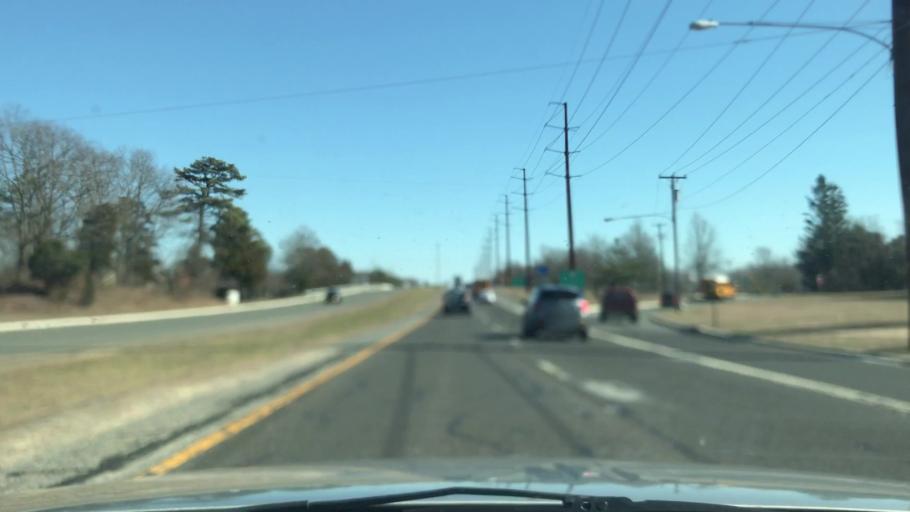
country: US
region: New Jersey
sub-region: Ocean County
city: Manahawkin
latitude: 39.6963
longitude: -74.2634
